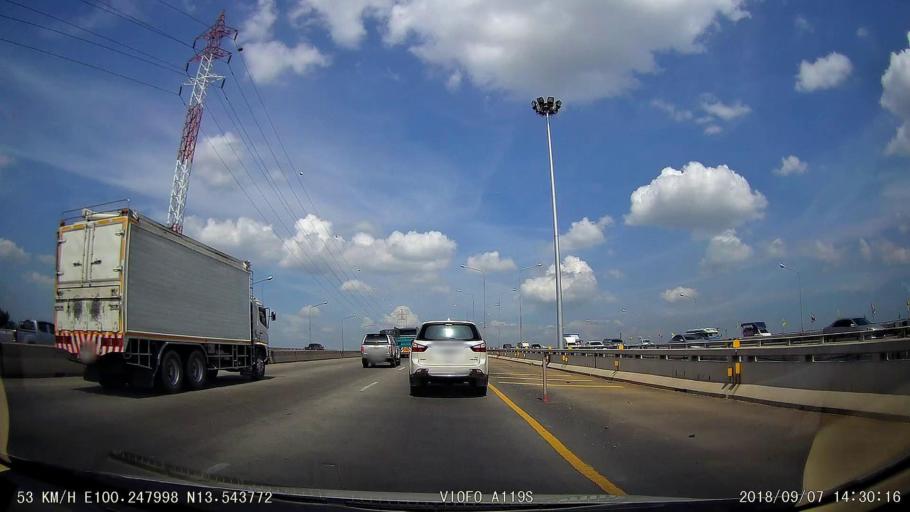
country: TH
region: Samut Sakhon
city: Samut Sakhon
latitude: 13.5442
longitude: 100.2491
